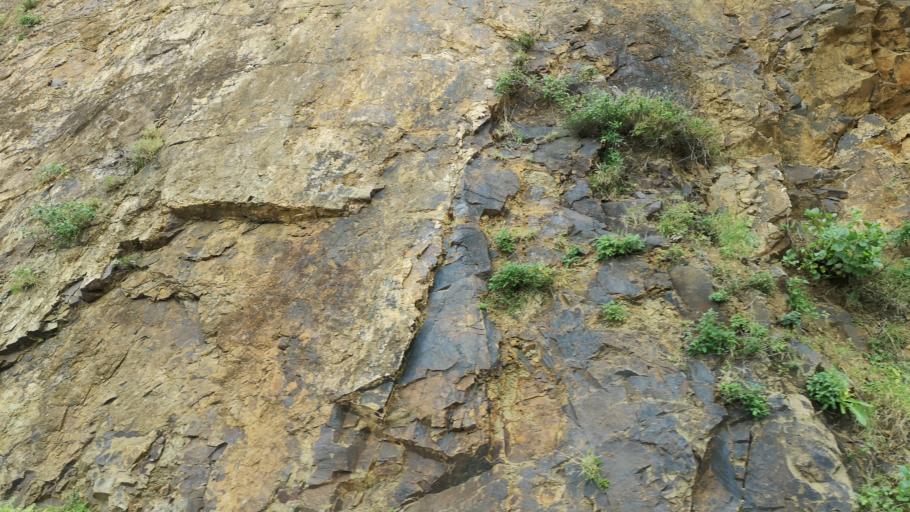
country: ES
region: Canary Islands
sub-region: Provincia de Santa Cruz de Tenerife
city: Agulo
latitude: 28.1876
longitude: -17.2103
